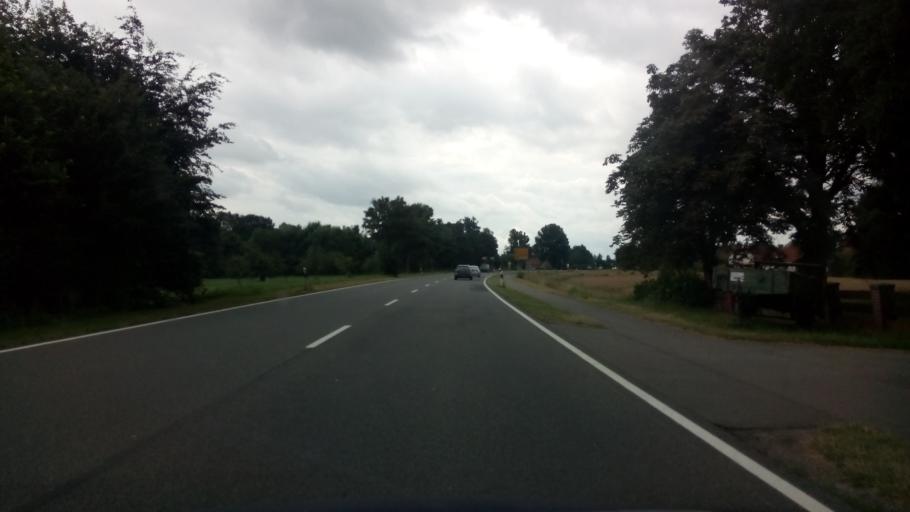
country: DE
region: Lower Saxony
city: Huede
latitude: 52.5112
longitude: 8.3763
